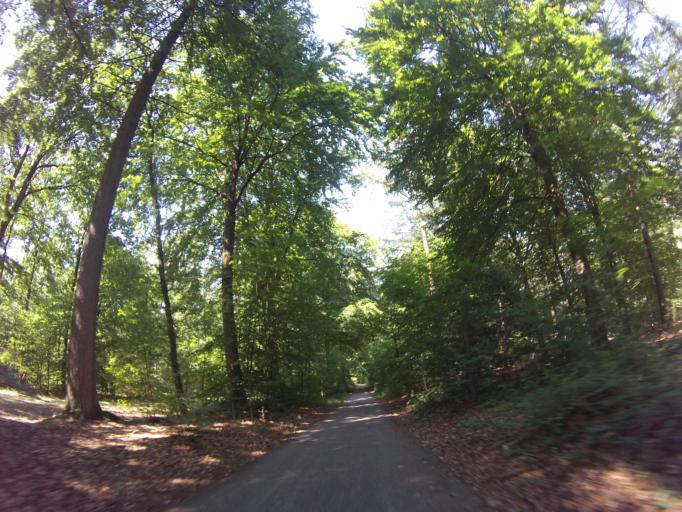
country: NL
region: Drenthe
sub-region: Gemeente Coevorden
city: Sleen
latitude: 52.8266
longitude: 6.7431
